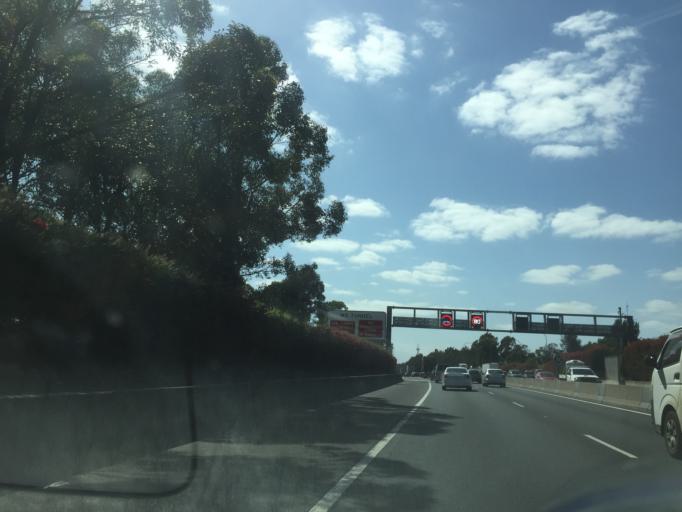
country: AU
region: New South Wales
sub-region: Canterbury
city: Clemton Park
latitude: -33.9404
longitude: 151.0903
